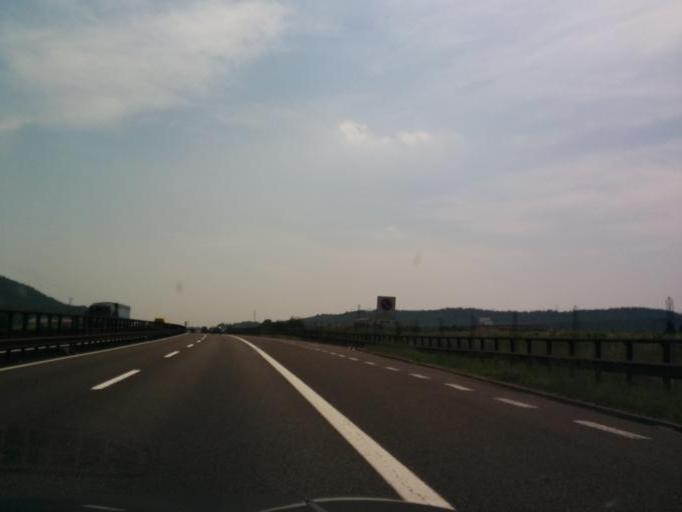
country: IT
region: Veneto
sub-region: Provincia di Verona
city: Rivoli Veronese
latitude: 45.5718
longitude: 10.8034
